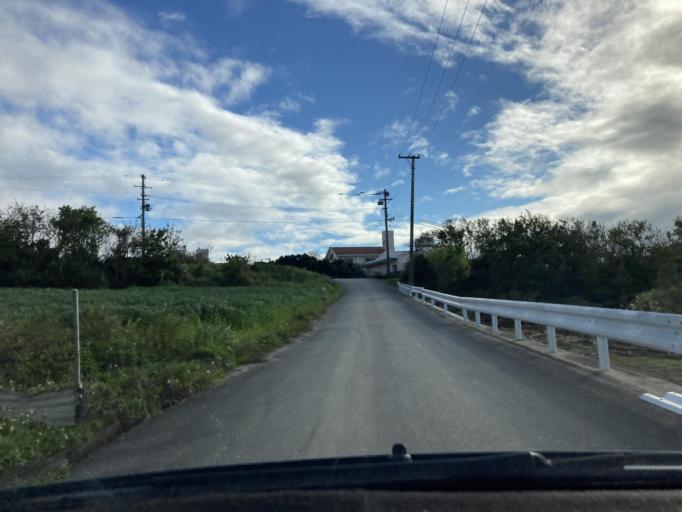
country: JP
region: Okinawa
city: Itoman
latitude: 26.1066
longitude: 127.6620
